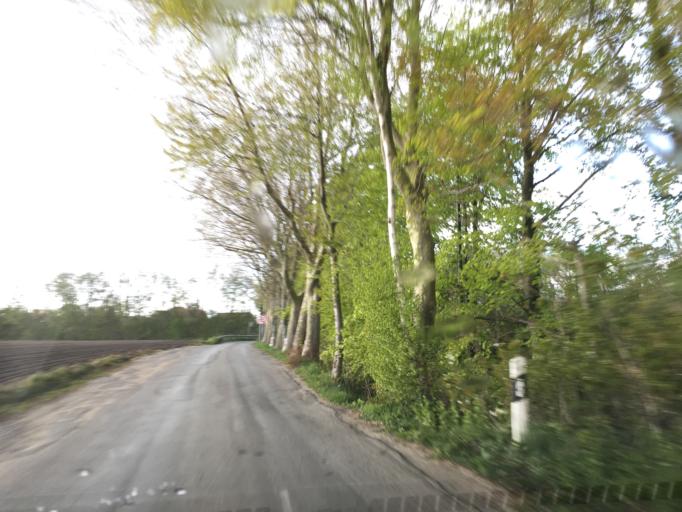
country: DE
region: North Rhine-Westphalia
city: Ludinghausen
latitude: 51.7832
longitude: 7.4660
